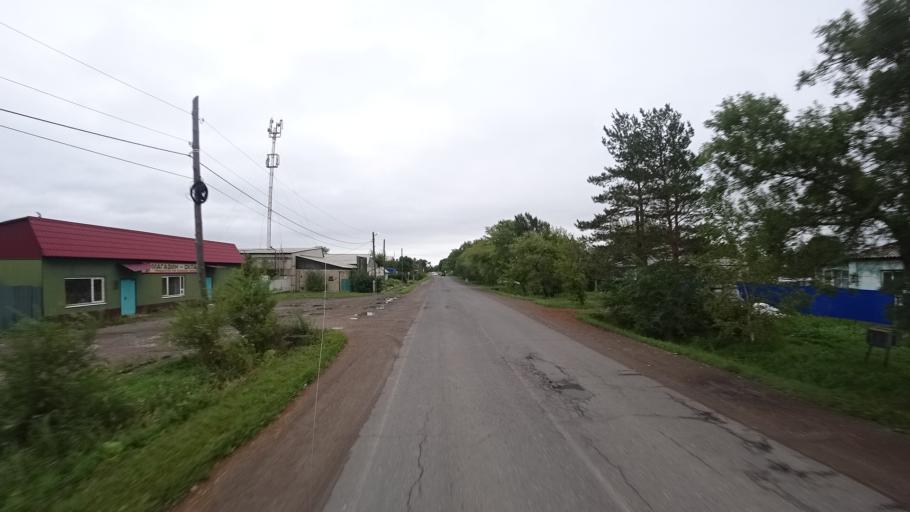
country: RU
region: Primorskiy
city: Chernigovka
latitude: 44.3463
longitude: 132.5542
